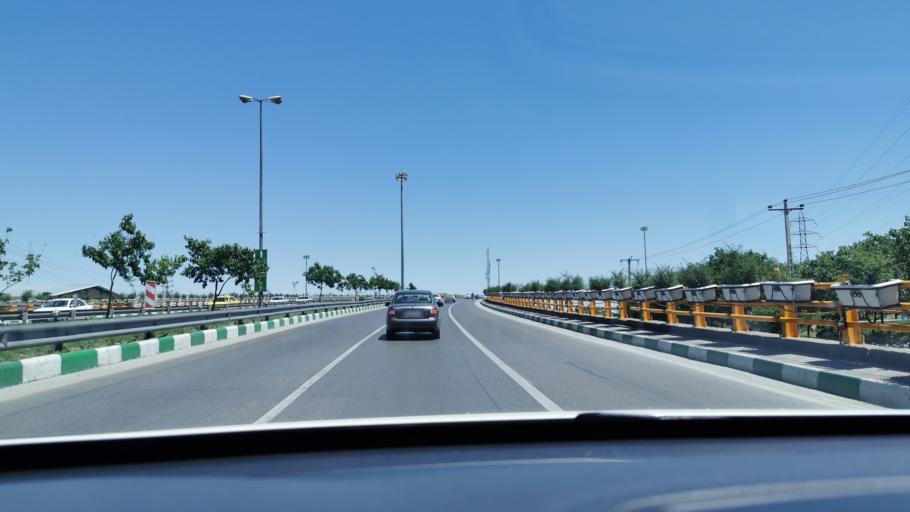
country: IR
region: Razavi Khorasan
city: Mashhad
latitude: 36.2566
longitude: 59.5962
